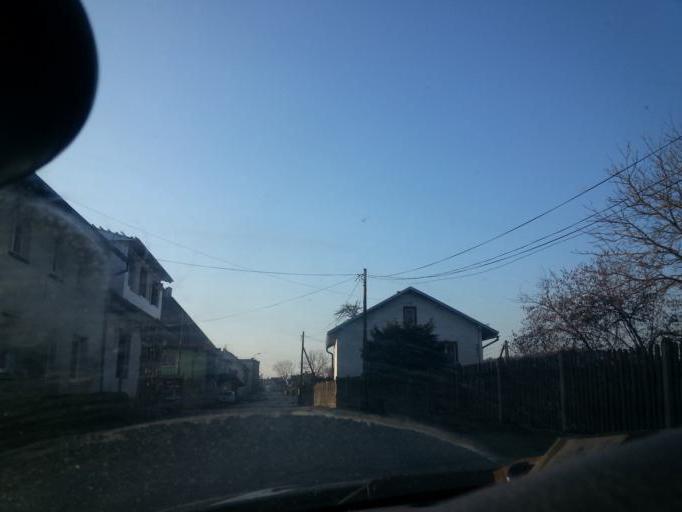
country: PL
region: Lower Silesian Voivodeship
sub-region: Powiat jeleniogorski
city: Myslakowice
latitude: 50.8194
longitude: 15.8071
